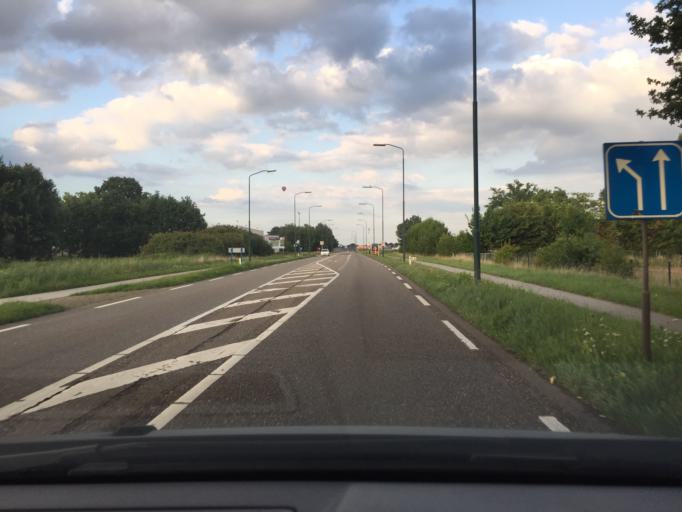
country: NL
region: North Brabant
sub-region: Gemeente Laarbeek
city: Aarle-Rixtel
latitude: 51.5228
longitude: 5.6214
